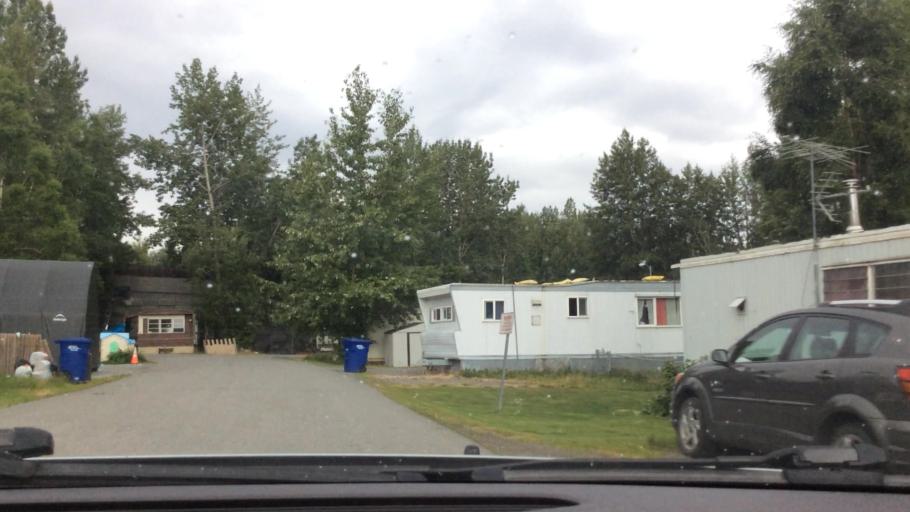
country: US
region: Alaska
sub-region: Anchorage Municipality
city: Anchorage
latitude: 61.1886
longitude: -149.7764
